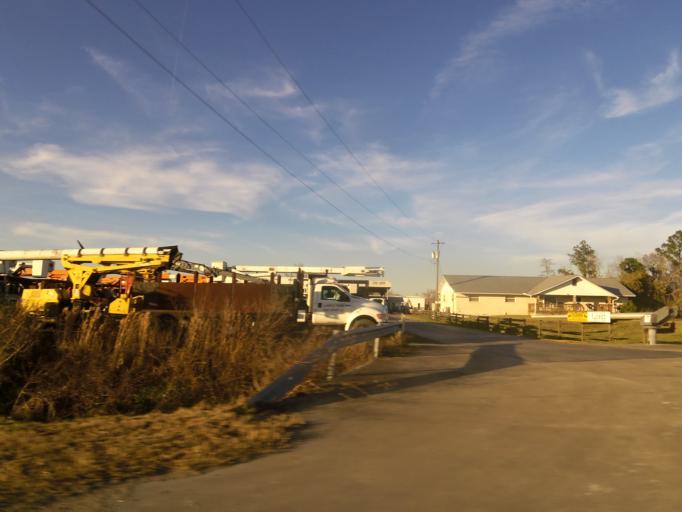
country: US
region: Florida
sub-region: Saint Johns County
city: Saint Augustine Shores
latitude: 29.7910
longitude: -81.4817
